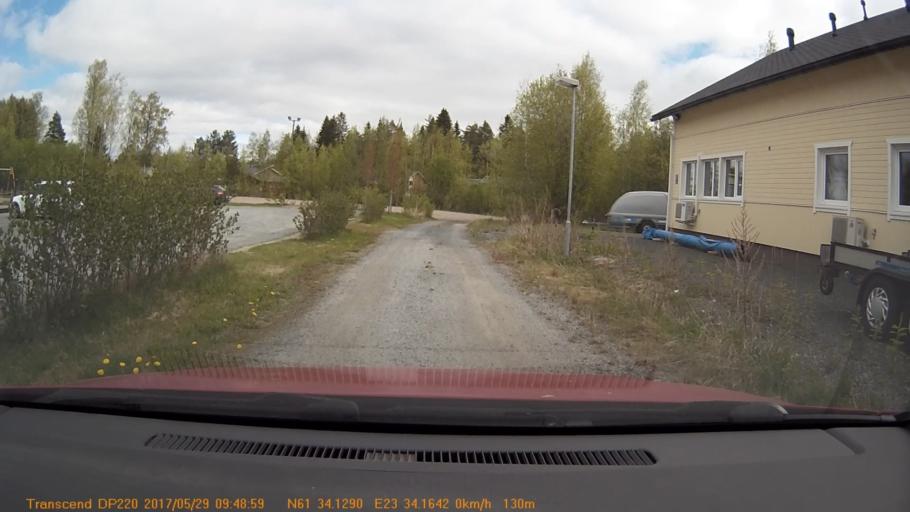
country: FI
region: Pirkanmaa
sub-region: Tampere
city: Yloejaervi
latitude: 61.5687
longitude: 23.5689
